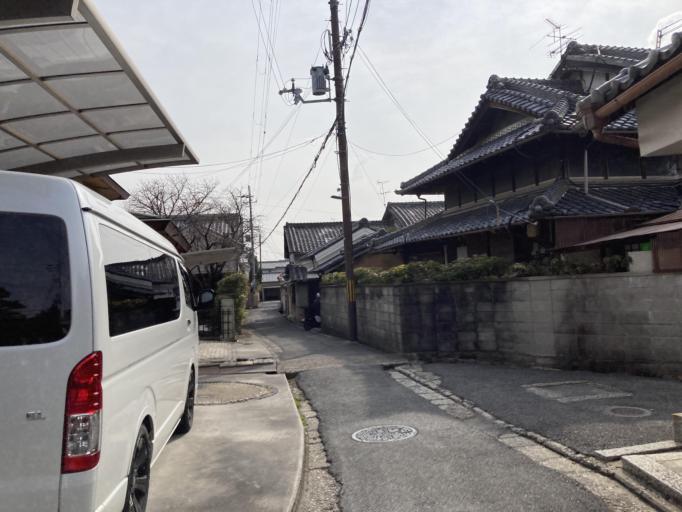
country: JP
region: Nara
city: Nara-shi
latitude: 34.6958
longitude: 135.7891
